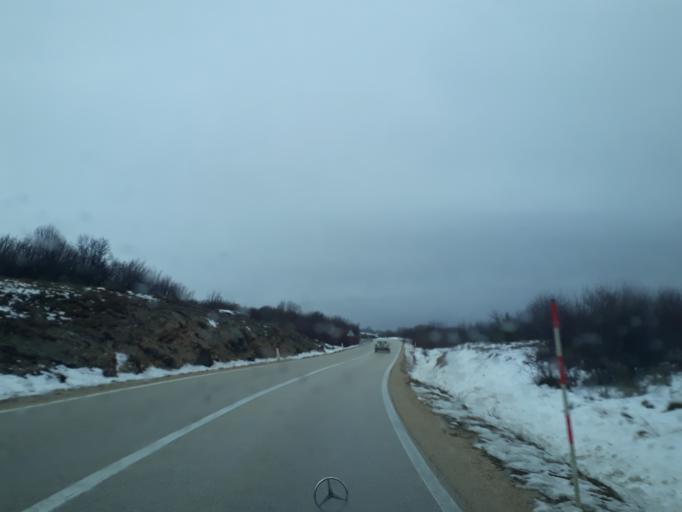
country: BA
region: Federation of Bosnia and Herzegovina
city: Tomislavgrad
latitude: 43.7971
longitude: 17.2138
